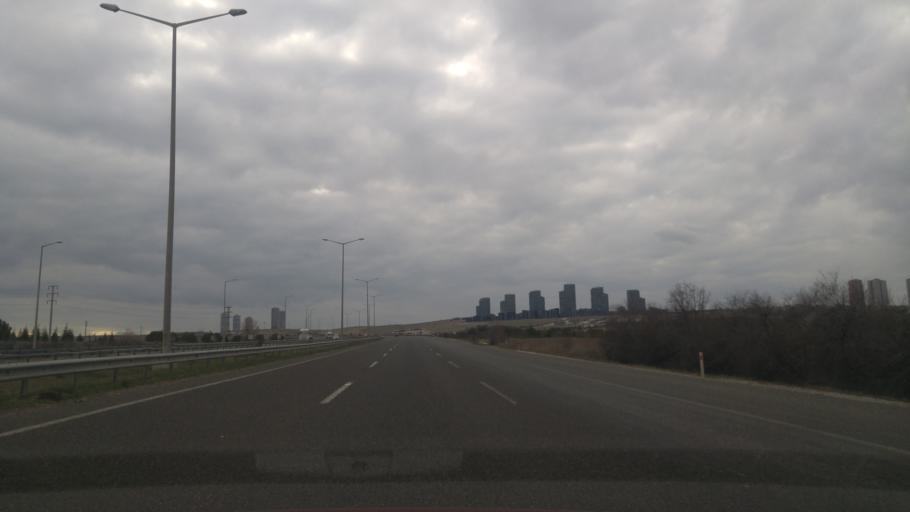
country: TR
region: Ankara
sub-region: Goelbasi
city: Golbasi
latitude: 39.7881
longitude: 32.7351
